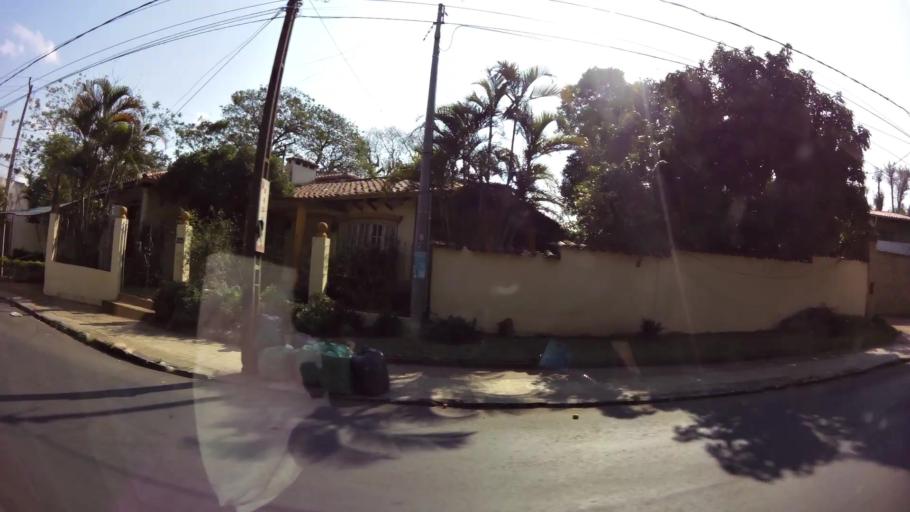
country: PY
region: Asuncion
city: Asuncion
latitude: -25.3118
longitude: -57.6311
